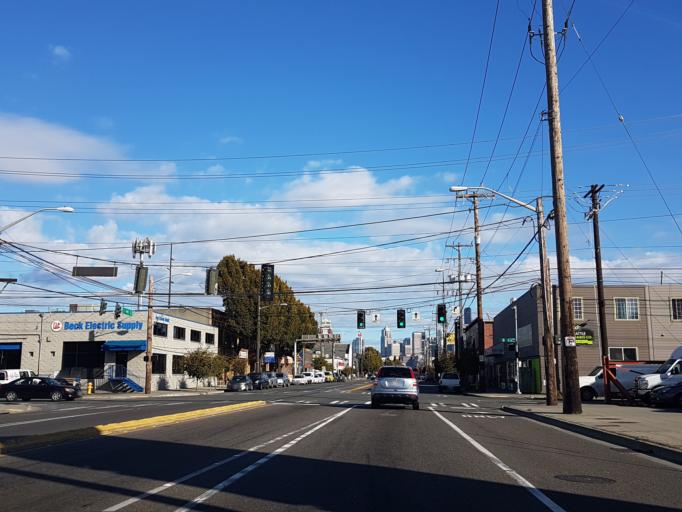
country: US
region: Washington
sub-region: King County
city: Seattle
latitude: 47.5740
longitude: -122.3341
